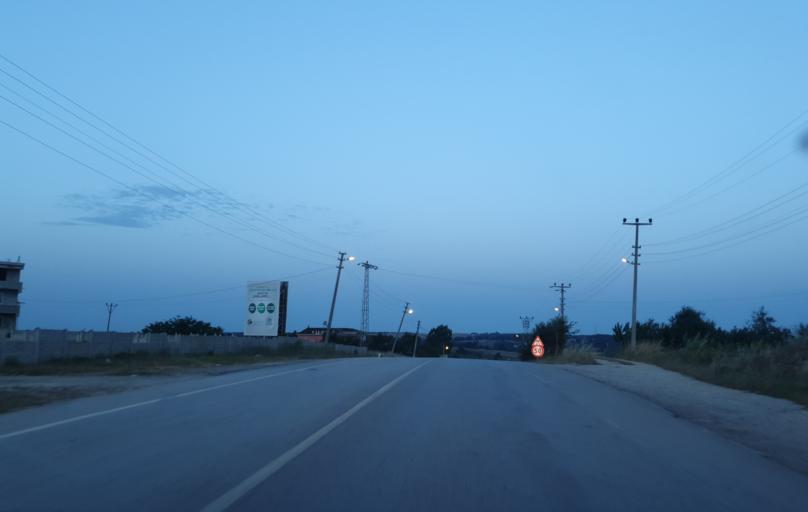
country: TR
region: Tekirdag
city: Saray
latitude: 41.3711
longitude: 27.9368
